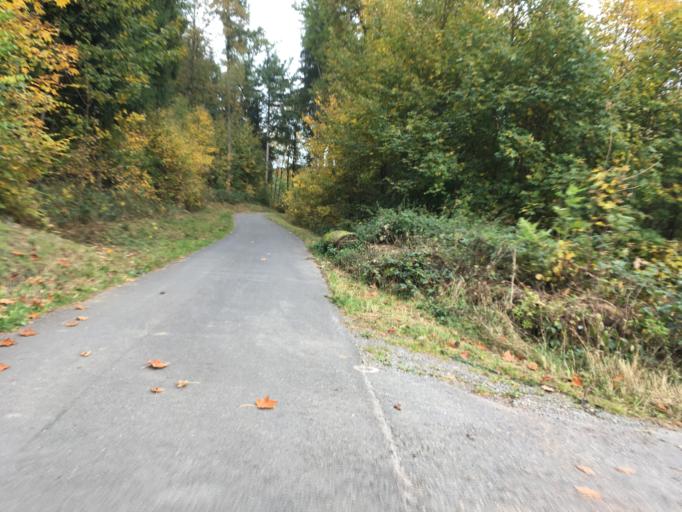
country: DE
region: Baden-Wuerttemberg
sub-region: Karlsruhe Region
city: Adelsheim
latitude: 49.4187
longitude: 9.3870
